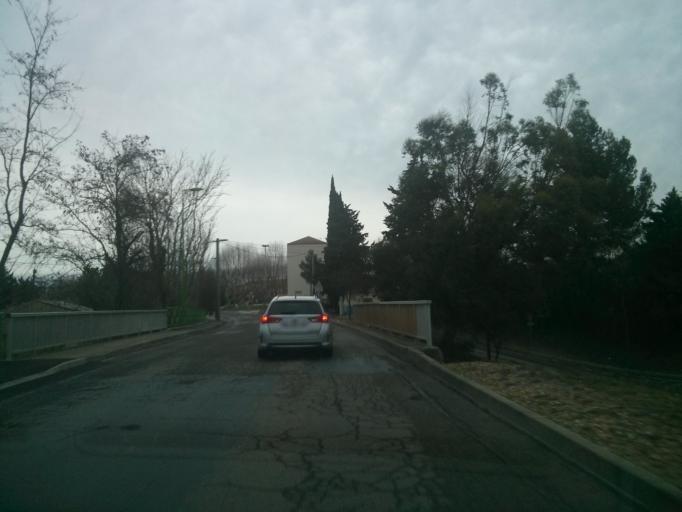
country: FR
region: Languedoc-Roussillon
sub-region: Departement du Gard
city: Saint-Gilles
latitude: 43.6713
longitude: 4.4289
